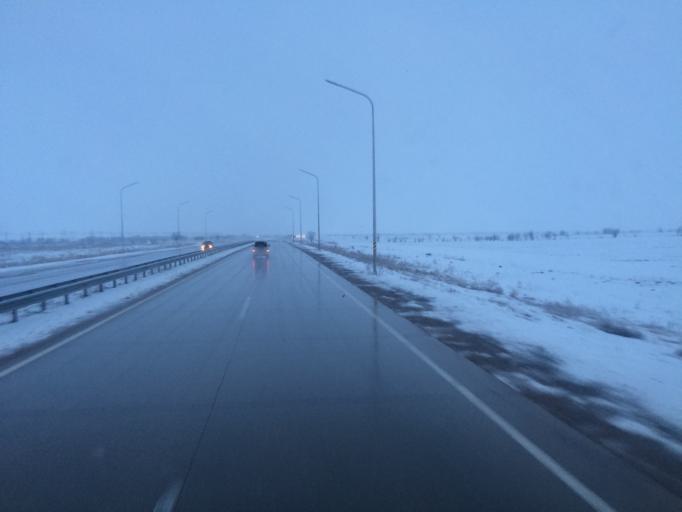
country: KZ
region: Zhambyl
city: Kulan
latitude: 42.9931
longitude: 72.3103
